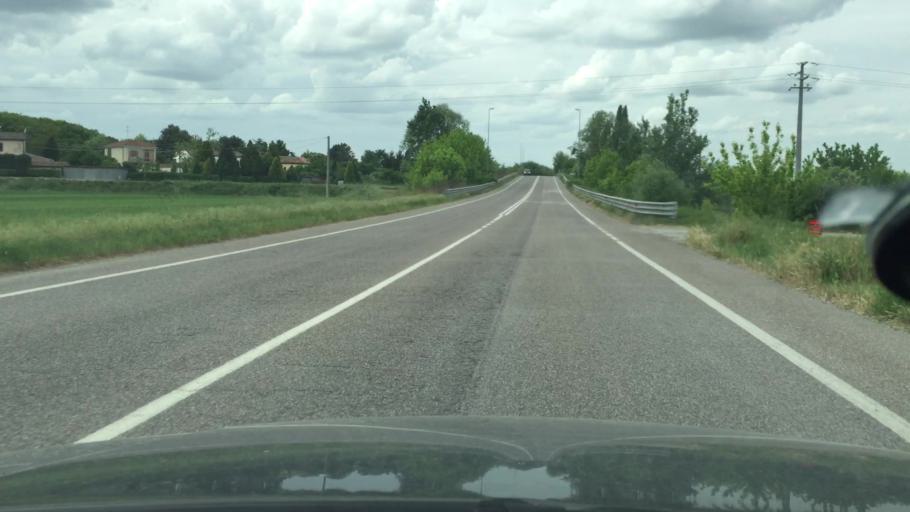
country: IT
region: Emilia-Romagna
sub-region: Provincia di Ferrara
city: Cona
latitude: 44.8107
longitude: 11.7157
